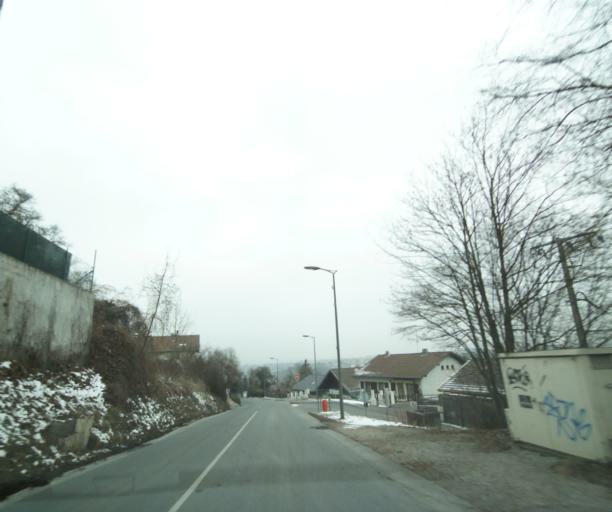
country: FR
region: Rhone-Alpes
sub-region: Departement de la Haute-Savoie
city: Vetraz-Monthoux
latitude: 46.1725
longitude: 6.2382
